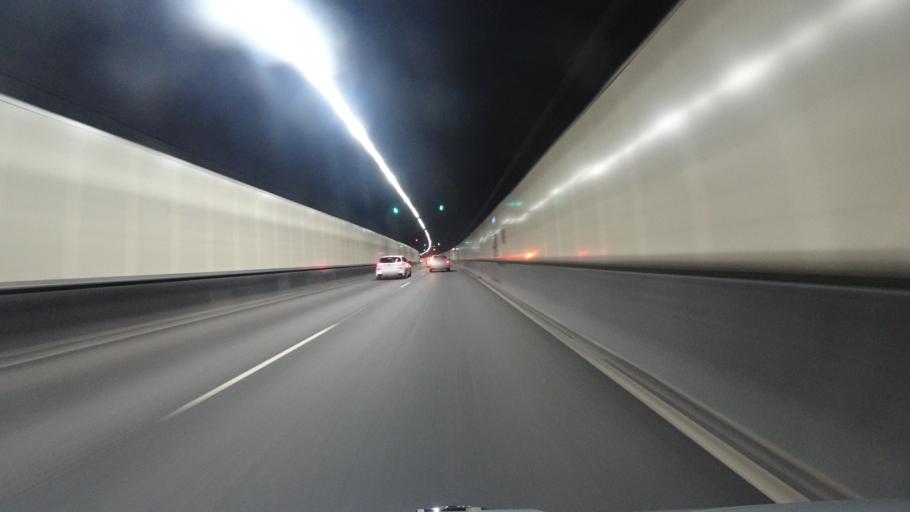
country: AU
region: New South Wales
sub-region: Rockdale
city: Bardwell Valley
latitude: -33.9367
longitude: 151.1259
